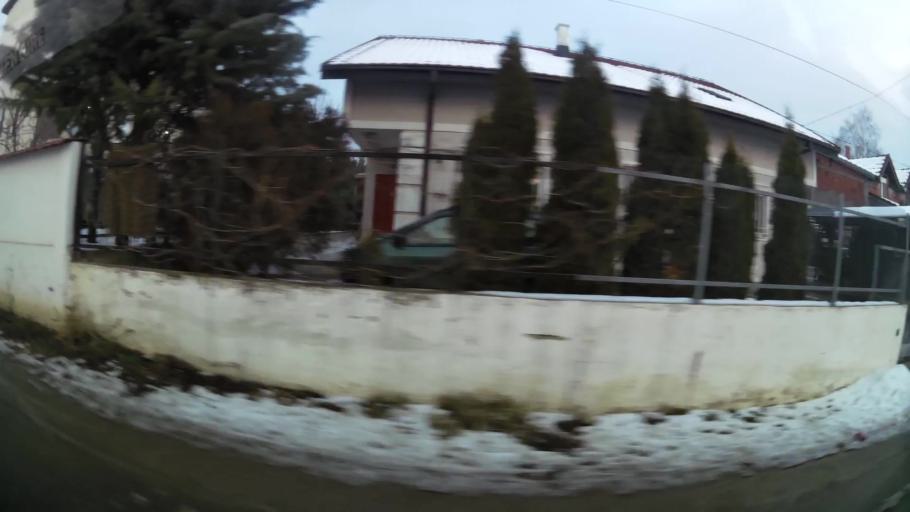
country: MK
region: Suto Orizari
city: Suto Orizare
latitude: 42.0387
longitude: 21.4076
